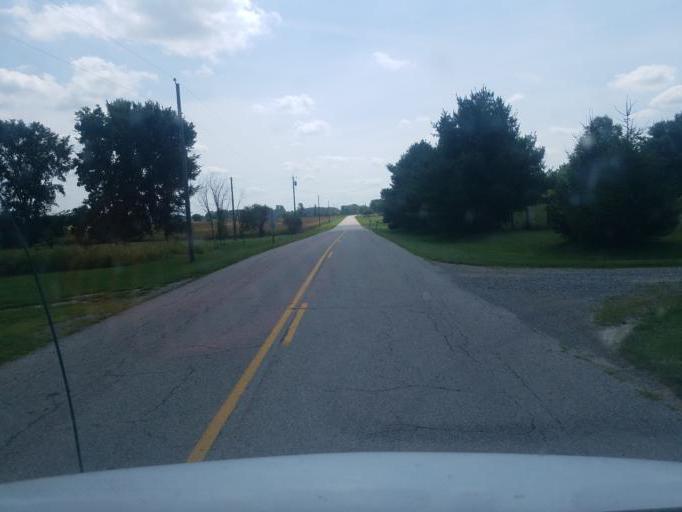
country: US
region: Ohio
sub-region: Union County
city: Marysville
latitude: 40.3135
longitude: -83.2930
